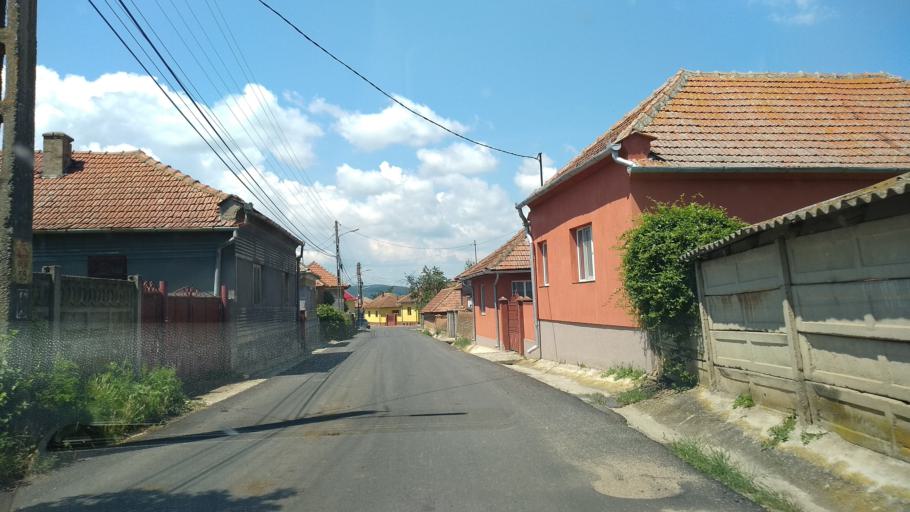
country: RO
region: Hunedoara
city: Berca
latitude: 45.6347
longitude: 23.0330
